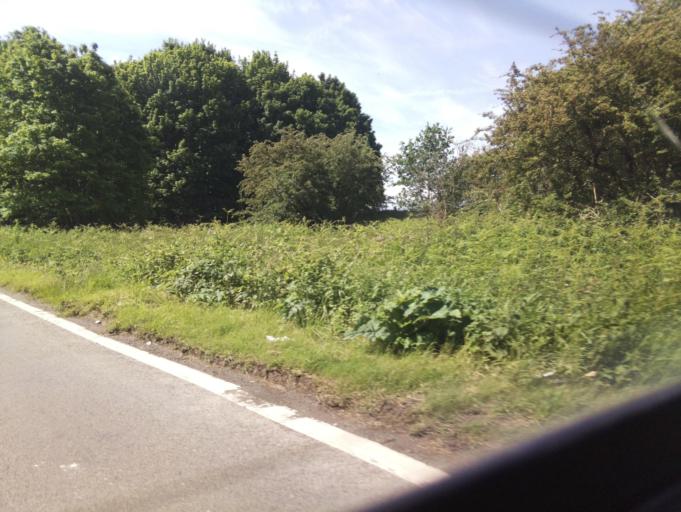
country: GB
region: England
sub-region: North Lincolnshire
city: Manton
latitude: 53.5196
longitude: -0.5801
